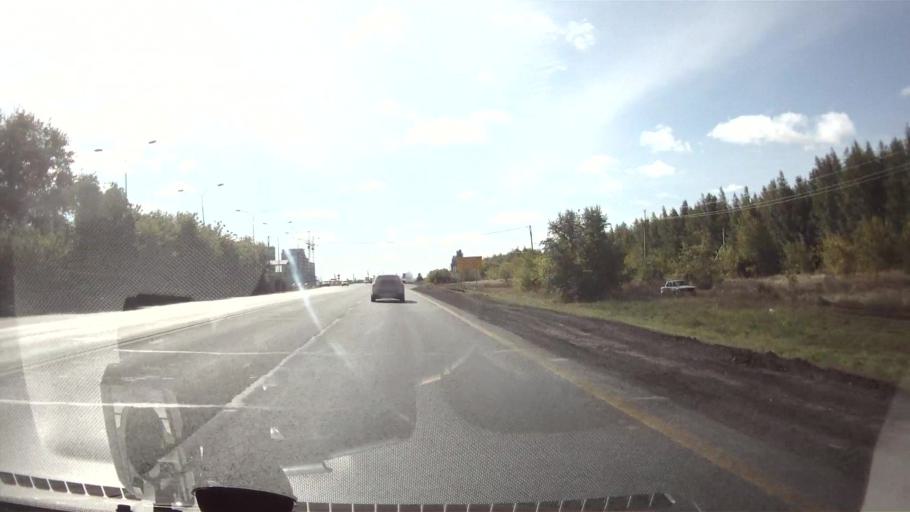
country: RU
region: Ulyanovsk
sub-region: Ulyanovskiy Rayon
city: Ulyanovsk
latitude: 54.2877
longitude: 48.2560
